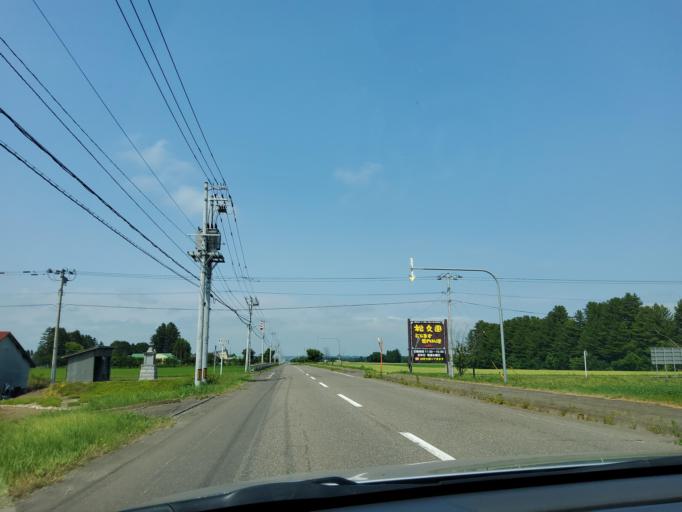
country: JP
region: Hokkaido
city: Obihiro
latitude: 42.8765
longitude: 143.0287
